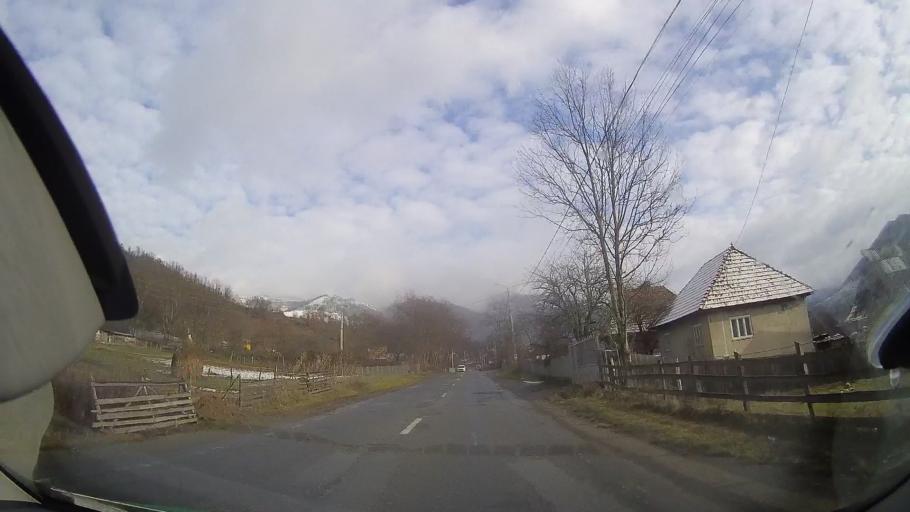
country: RO
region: Alba
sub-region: Comuna Lupsa
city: Lupsa
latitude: 46.3772
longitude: 23.2195
